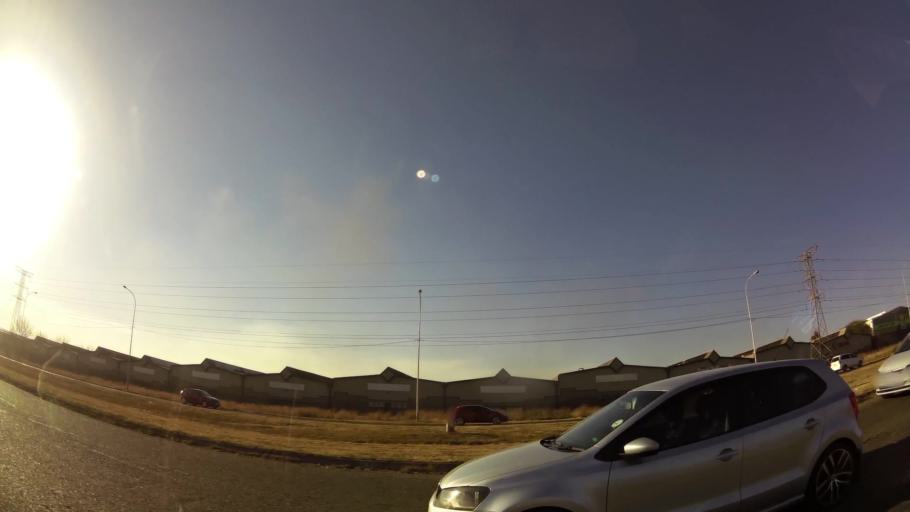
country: ZA
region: Gauteng
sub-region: City of Johannesburg Metropolitan Municipality
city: Roodepoort
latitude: -26.1899
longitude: 27.9144
